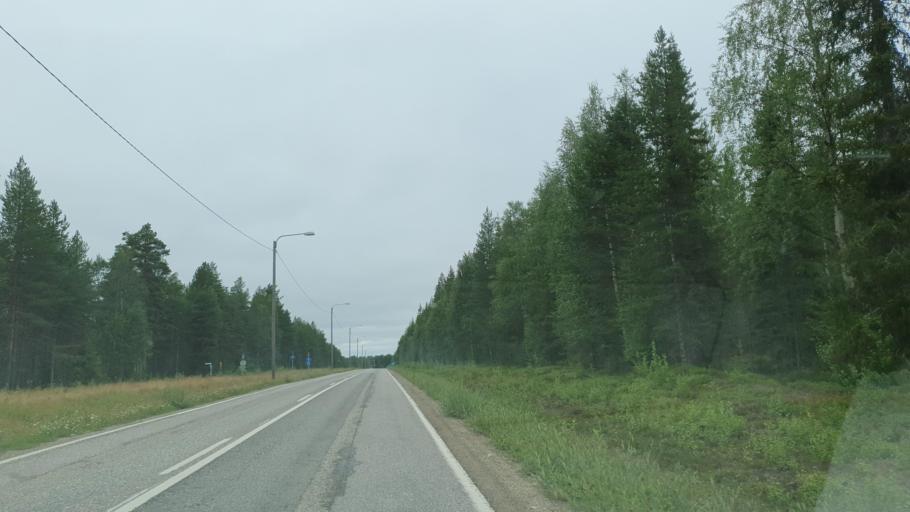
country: FI
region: Lapland
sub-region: Pohjois-Lappi
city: Sodankylae
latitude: 67.4095
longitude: 26.6306
